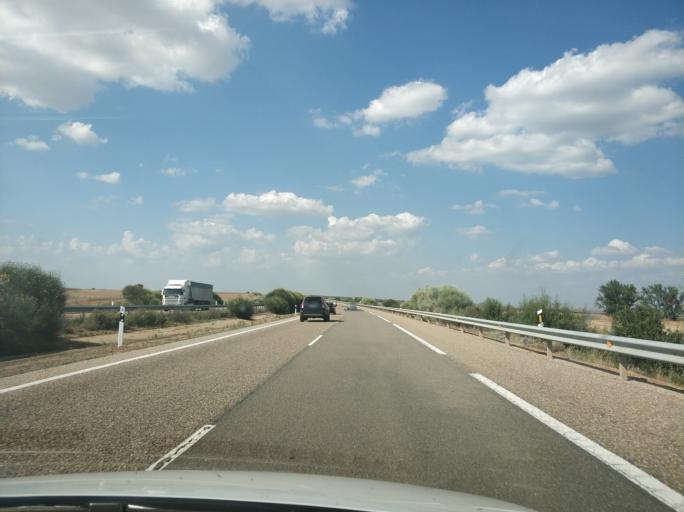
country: ES
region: Castille and Leon
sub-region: Provincia de Zamora
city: Matilla de Arzon
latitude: 42.0771
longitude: -5.6568
